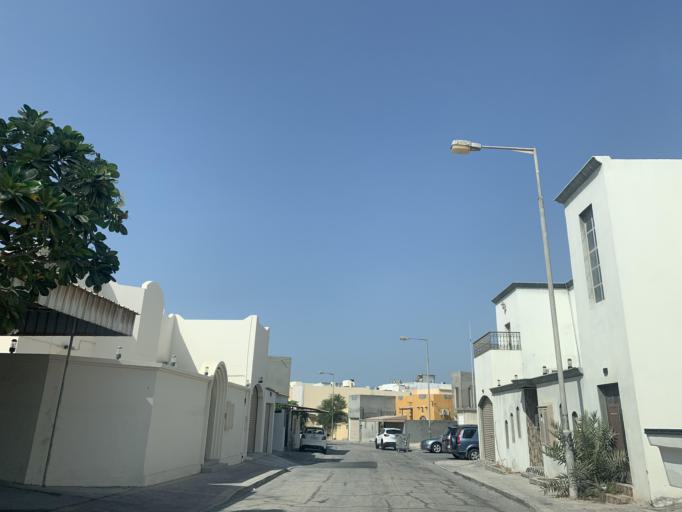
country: BH
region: Central Governorate
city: Madinat Hamad
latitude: 26.1301
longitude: 50.5035
